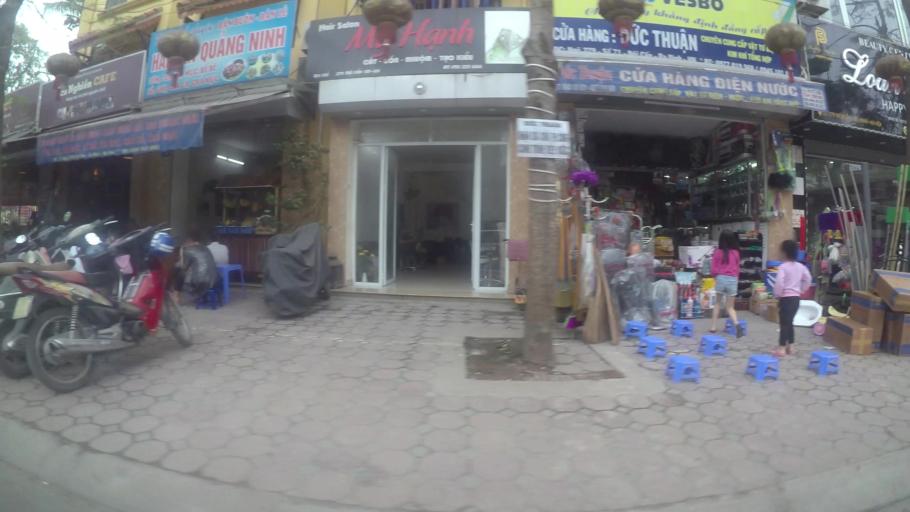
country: VN
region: Ha Noi
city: Dong Da
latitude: 21.0368
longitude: 105.8204
